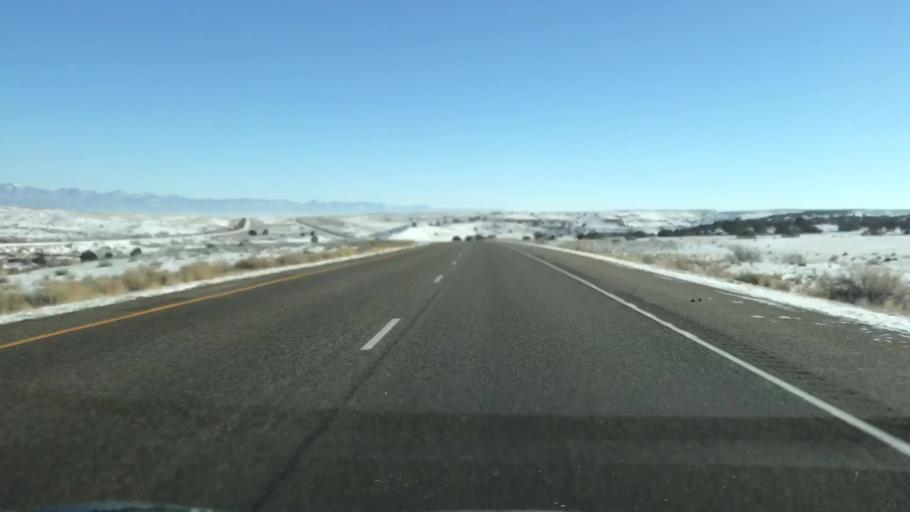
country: US
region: Colorado
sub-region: Mesa County
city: Loma
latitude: 39.2210
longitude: -108.9503
